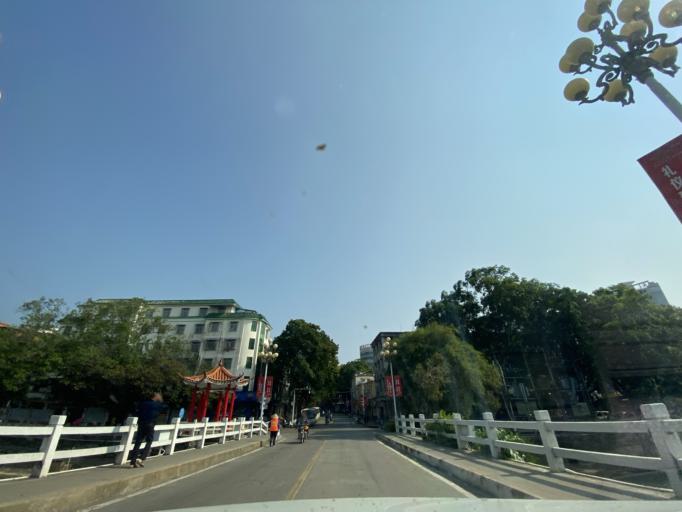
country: CN
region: Hainan
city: Chongshan
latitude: 18.7812
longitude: 109.5115
